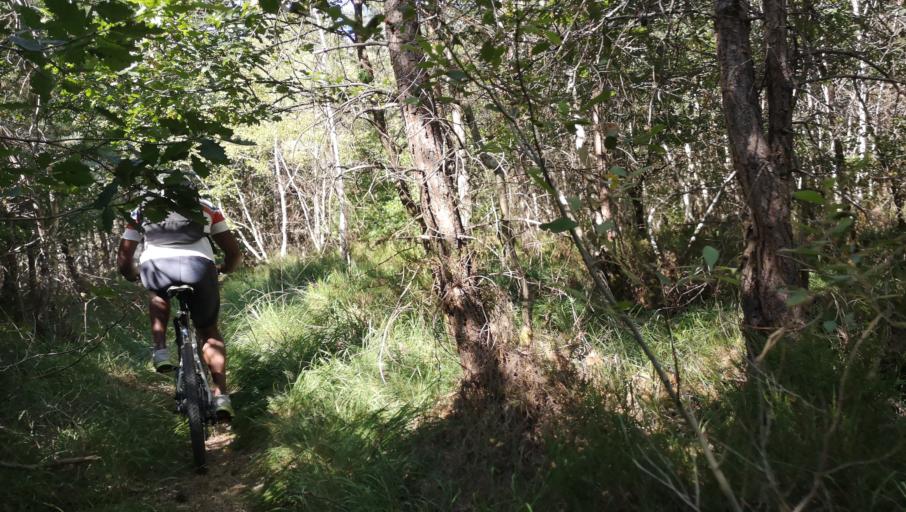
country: FR
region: Centre
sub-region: Departement du Loiret
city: Semoy
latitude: 47.9494
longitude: 1.9560
